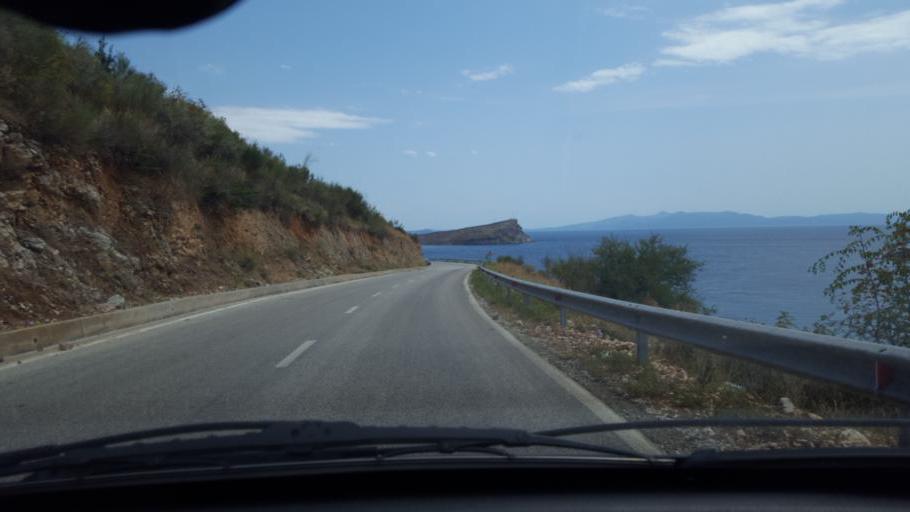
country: AL
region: Vlore
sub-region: Rrethi i Vlores
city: Himare
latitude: 40.0751
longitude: 19.7792
